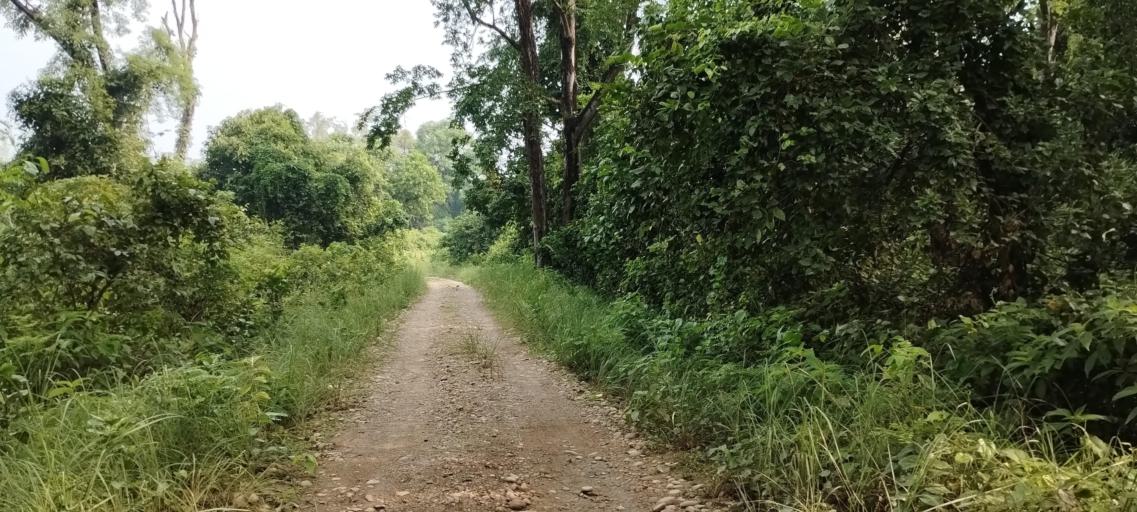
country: NP
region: Far Western
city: Tikapur
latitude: 28.4571
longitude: 81.2424
